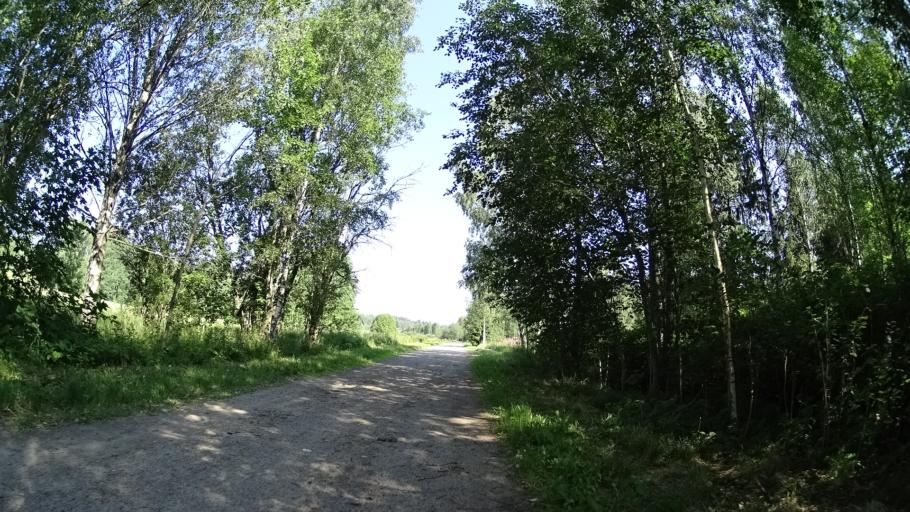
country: FI
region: Uusimaa
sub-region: Helsinki
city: Kerava
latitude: 60.3569
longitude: 25.1253
